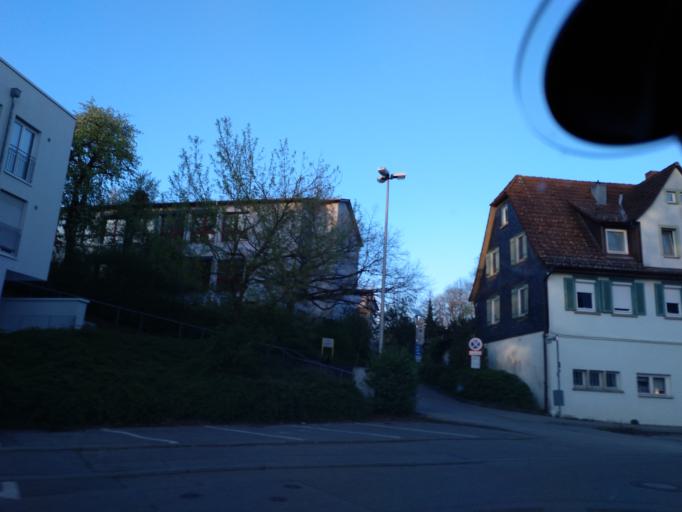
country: DE
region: Baden-Wuerttemberg
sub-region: Regierungsbezirk Stuttgart
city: Crailsheim
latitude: 49.1408
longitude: 10.0700
